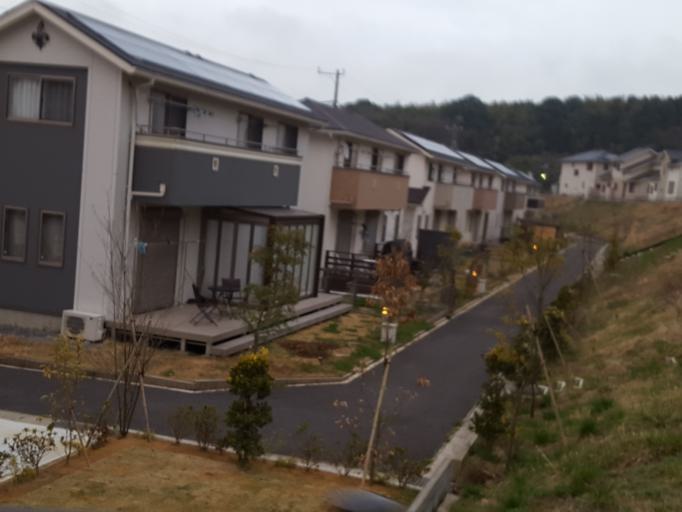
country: JP
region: Chiba
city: Ichihara
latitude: 35.4545
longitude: 140.0534
